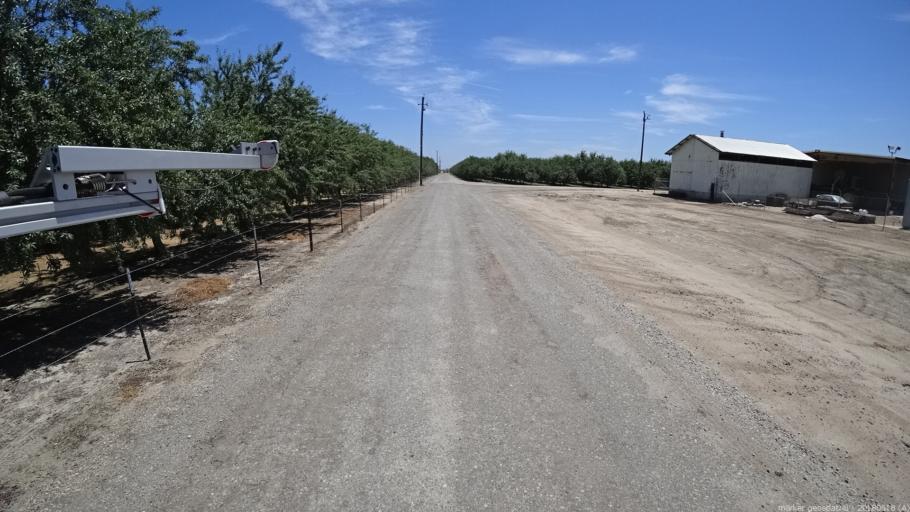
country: US
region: California
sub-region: Madera County
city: Parkwood
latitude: 36.9020
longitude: -120.0957
